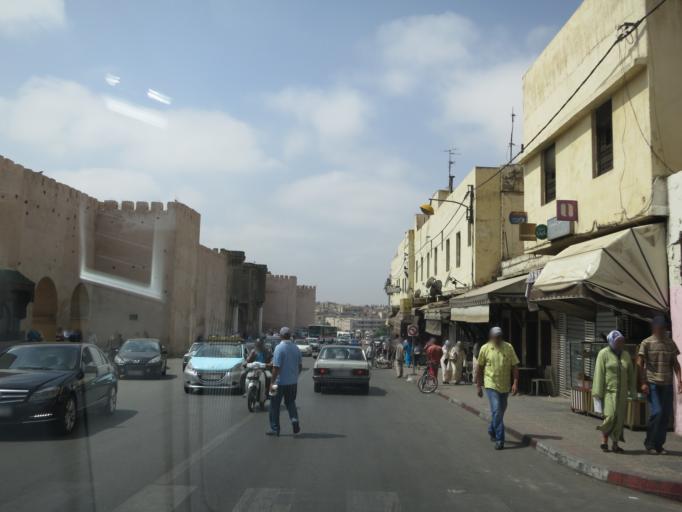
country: MA
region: Meknes-Tafilalet
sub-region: Meknes
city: Meknes
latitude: 33.8934
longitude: -5.5639
